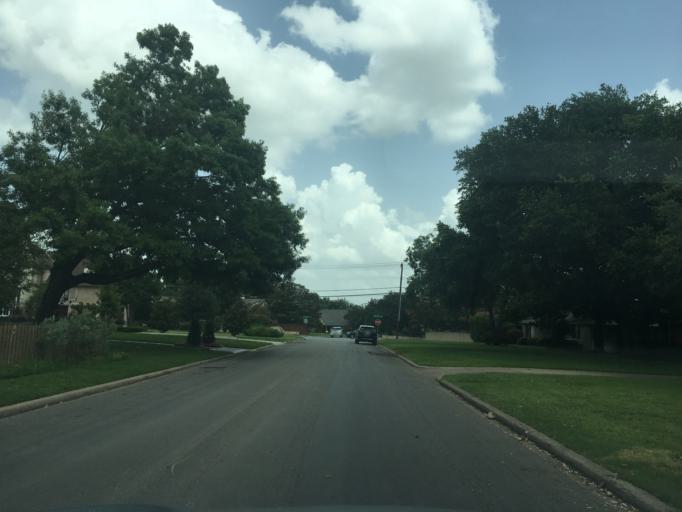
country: US
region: Texas
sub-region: Dallas County
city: University Park
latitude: 32.8915
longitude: -96.7880
